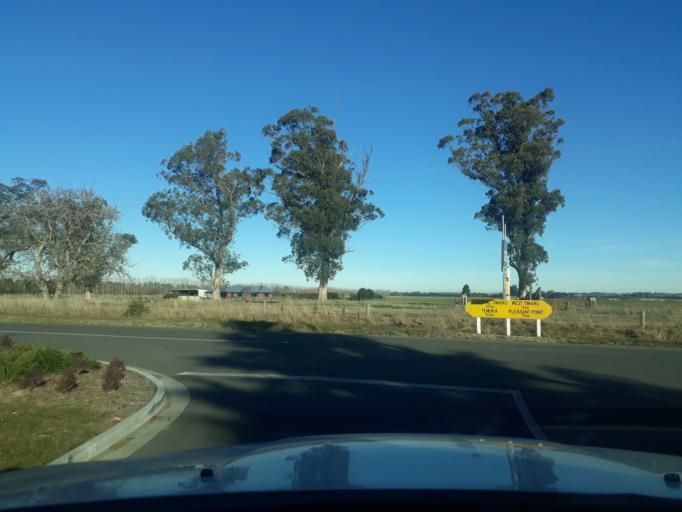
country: NZ
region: Canterbury
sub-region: Timaru District
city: Timaru
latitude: -44.3094
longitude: 171.2259
